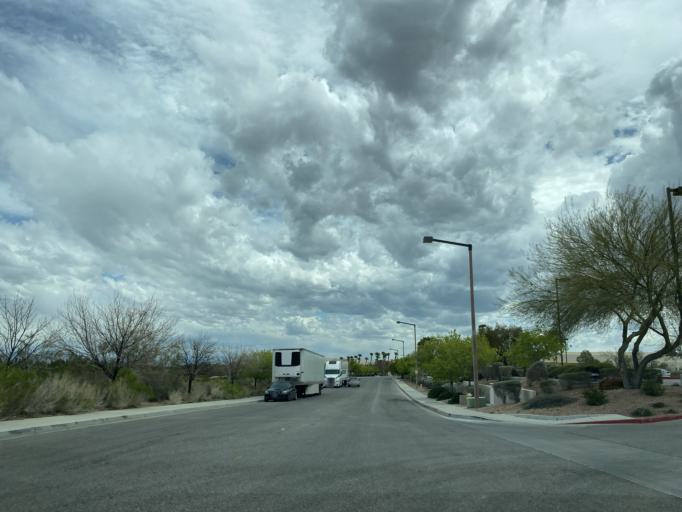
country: US
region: Nevada
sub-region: Clark County
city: Summerlin South
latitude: 36.1894
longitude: -115.3139
